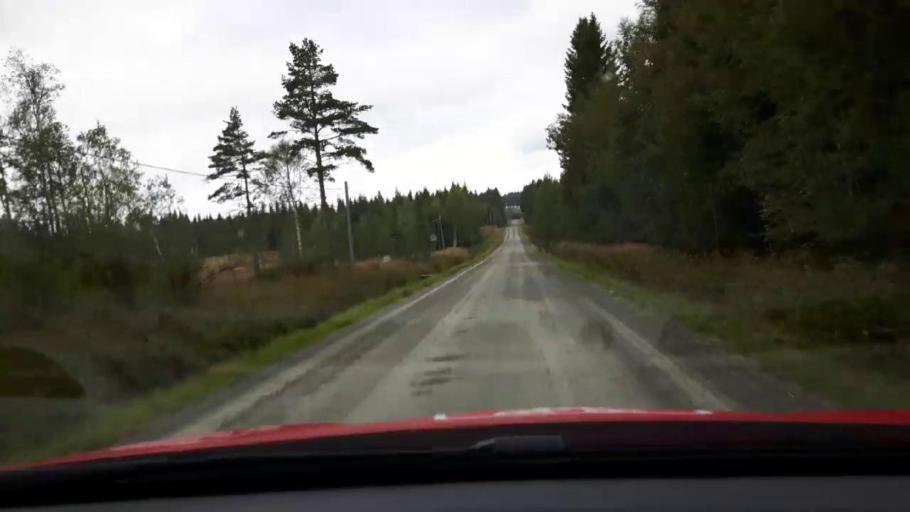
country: SE
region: Jaemtland
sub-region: Bergs Kommun
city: Hoverberg
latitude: 62.8581
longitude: 14.3124
